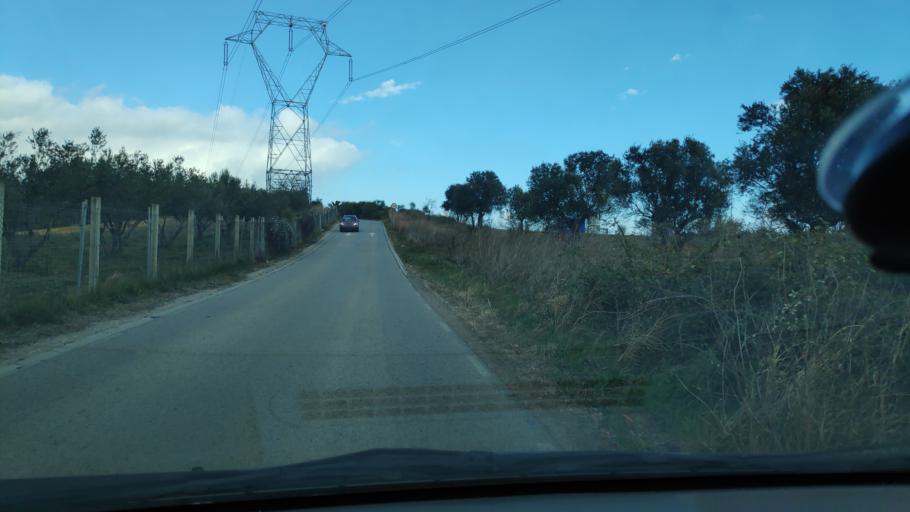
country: ES
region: Catalonia
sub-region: Provincia de Barcelona
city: Terrassa
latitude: 41.5795
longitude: 1.9877
